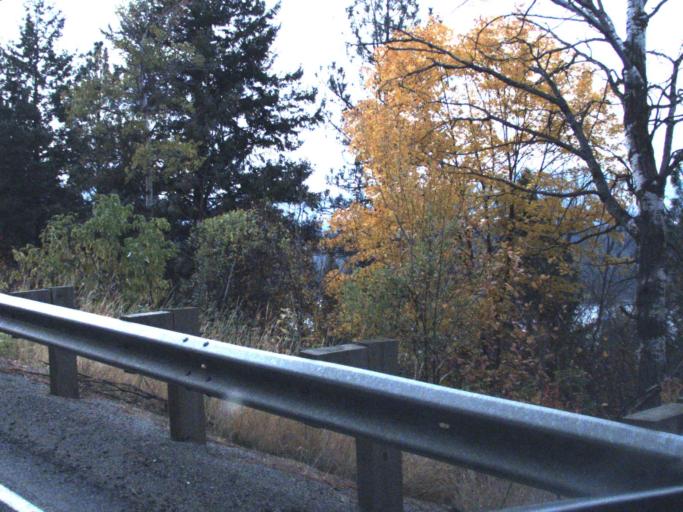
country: US
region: Washington
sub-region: Stevens County
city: Kettle Falls
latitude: 48.1414
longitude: -118.1897
